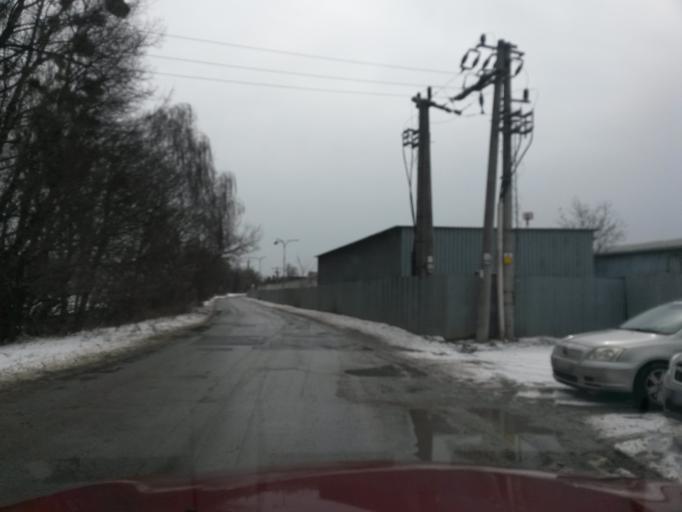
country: SK
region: Kosicky
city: Kosice
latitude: 48.7114
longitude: 21.2695
